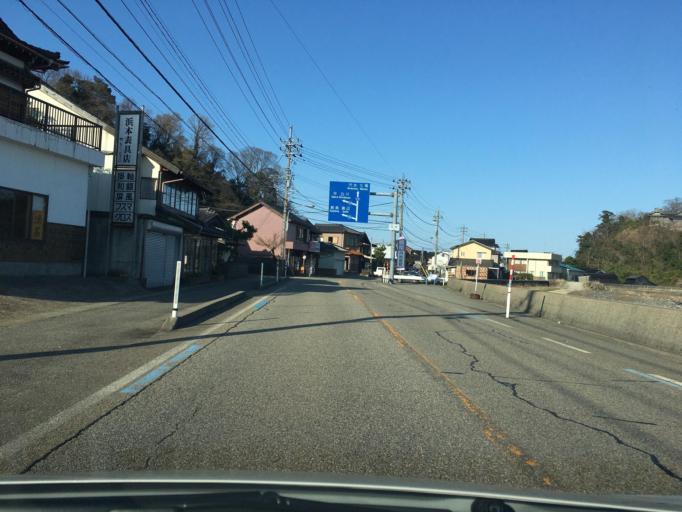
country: JP
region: Toyama
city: Himi
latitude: 36.8794
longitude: 136.9865
